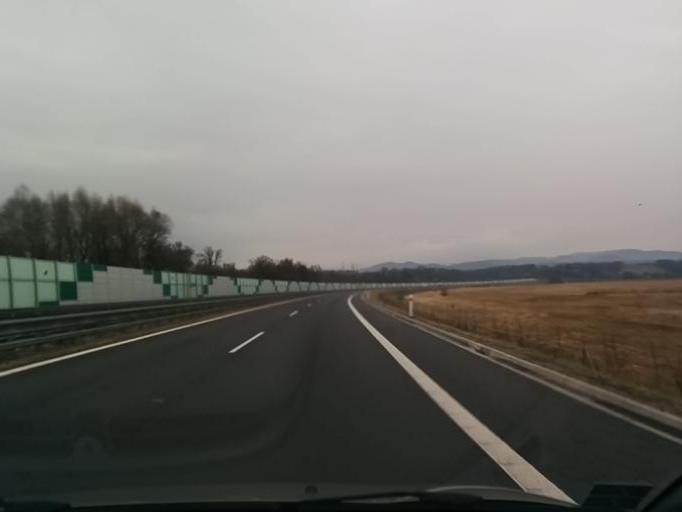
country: SK
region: Banskobystricky
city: Ziar nad Hronom
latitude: 48.5670
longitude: 18.8206
